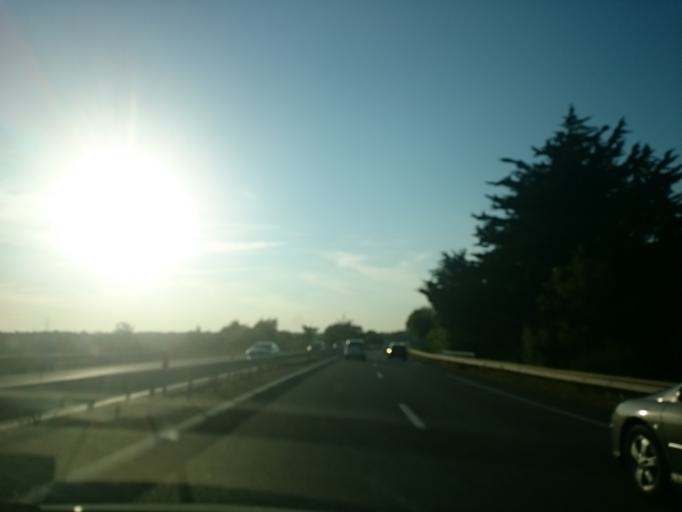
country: FR
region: Brittany
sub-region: Departement du Morbihan
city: Muzillac
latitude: 47.5496
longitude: -2.4807
